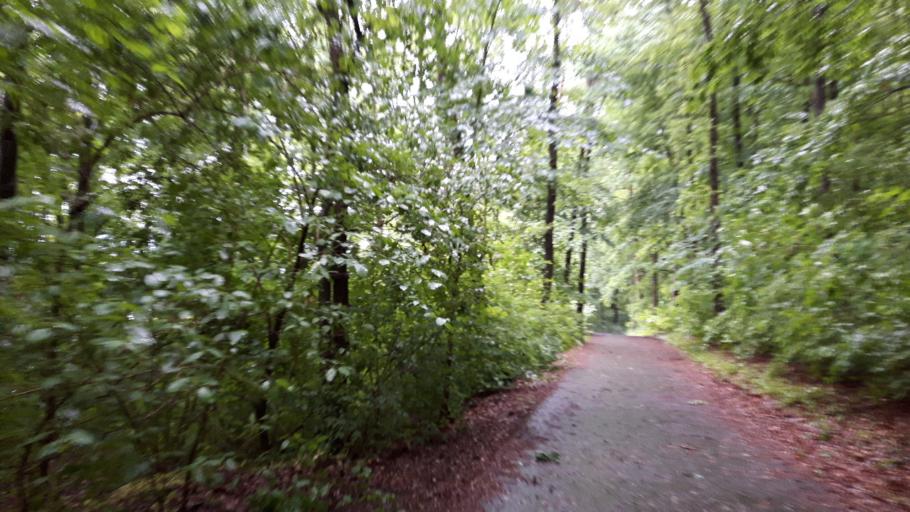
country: DE
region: Thuringia
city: Veilsdorf
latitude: 50.4105
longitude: 10.8181
